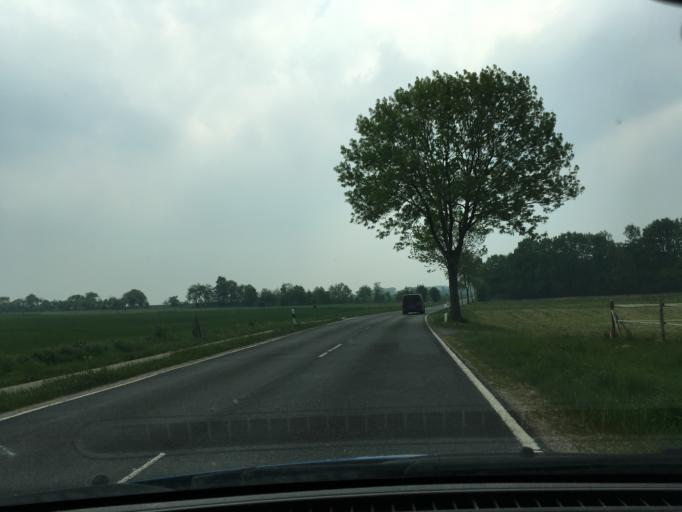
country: DE
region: Lower Saxony
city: Buchholz in der Nordheide
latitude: 53.3949
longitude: 9.8594
